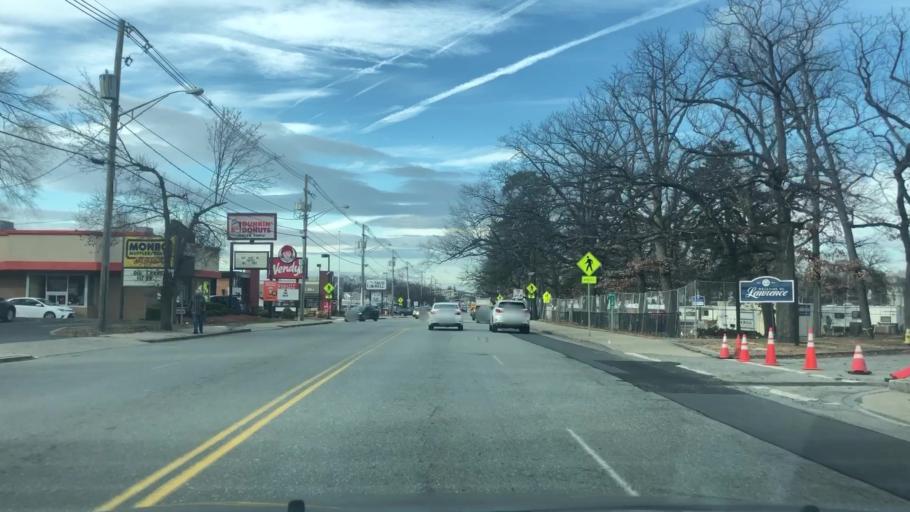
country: US
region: Massachusetts
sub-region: Essex County
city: North Andover
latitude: 42.6888
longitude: -71.1475
